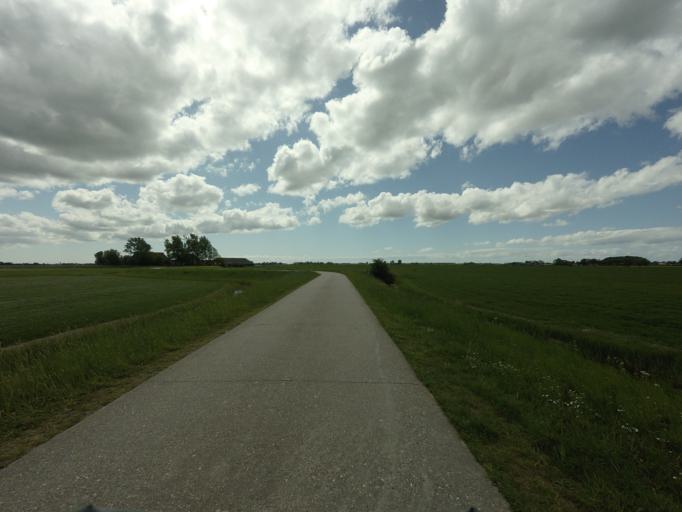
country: NL
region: Friesland
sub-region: Gemeente Littenseradiel
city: Wommels
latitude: 53.1213
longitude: 5.5539
